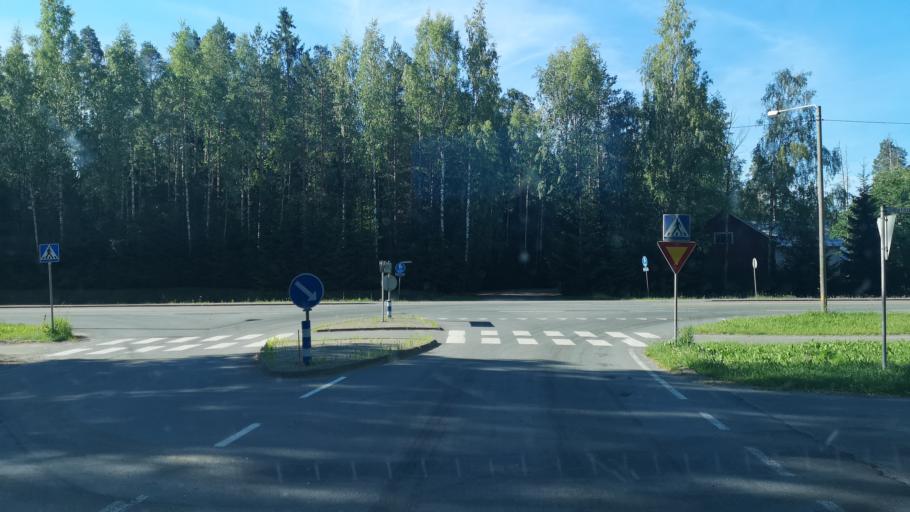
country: FI
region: Southern Ostrobothnia
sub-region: Seinaejoki
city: Lapua
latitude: 62.9697
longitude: 23.0540
